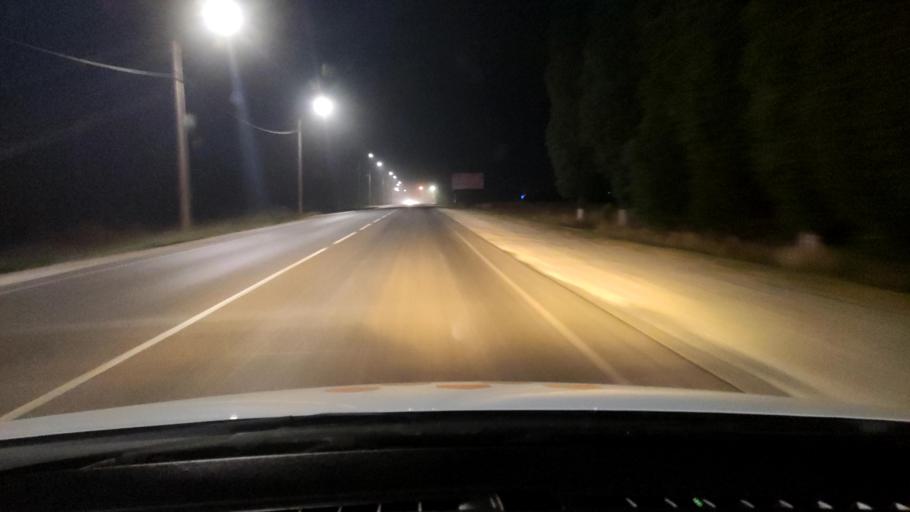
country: RU
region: Voronezj
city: Semiluki
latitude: 51.7212
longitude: 39.0332
